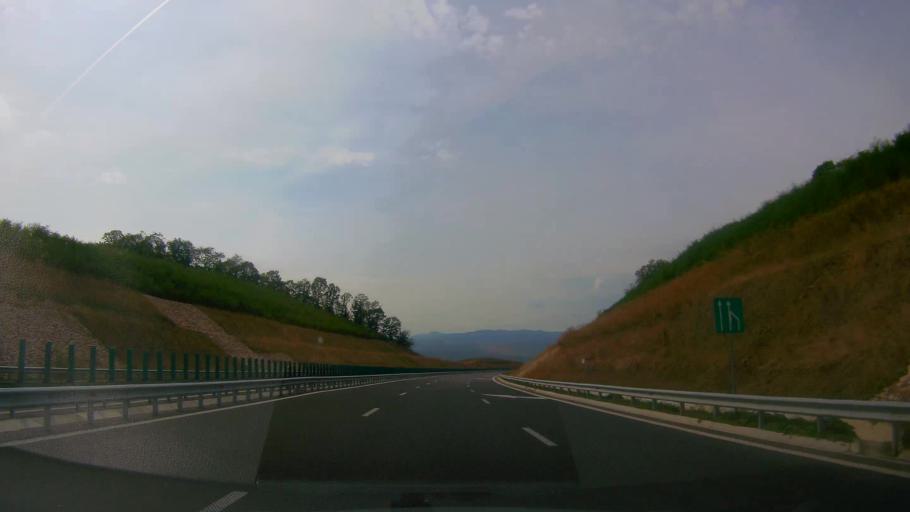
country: RO
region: Cluj
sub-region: Comuna Floresti
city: Luna de Sus
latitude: 46.7825
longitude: 23.4157
